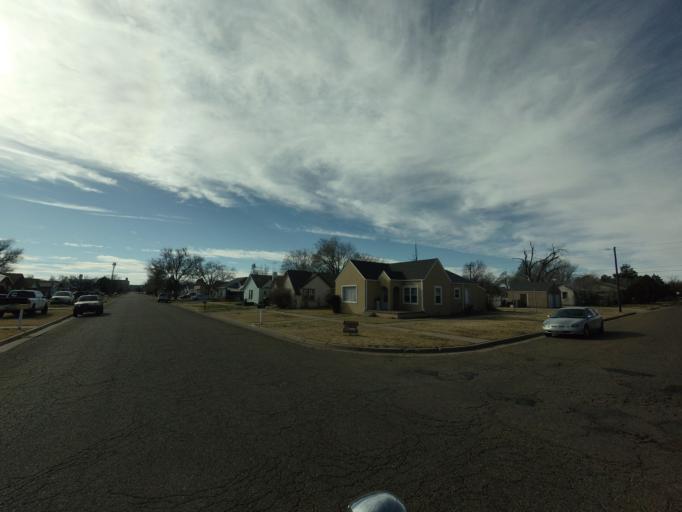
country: US
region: New Mexico
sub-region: Curry County
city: Clovis
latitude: 34.4099
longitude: -103.2003
